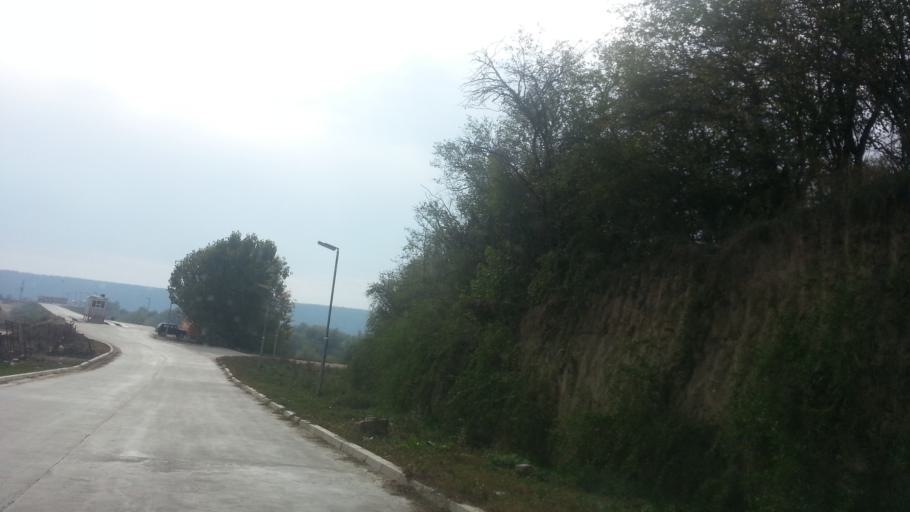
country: RS
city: Stari Banovci
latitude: 45.0009
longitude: 20.3038
